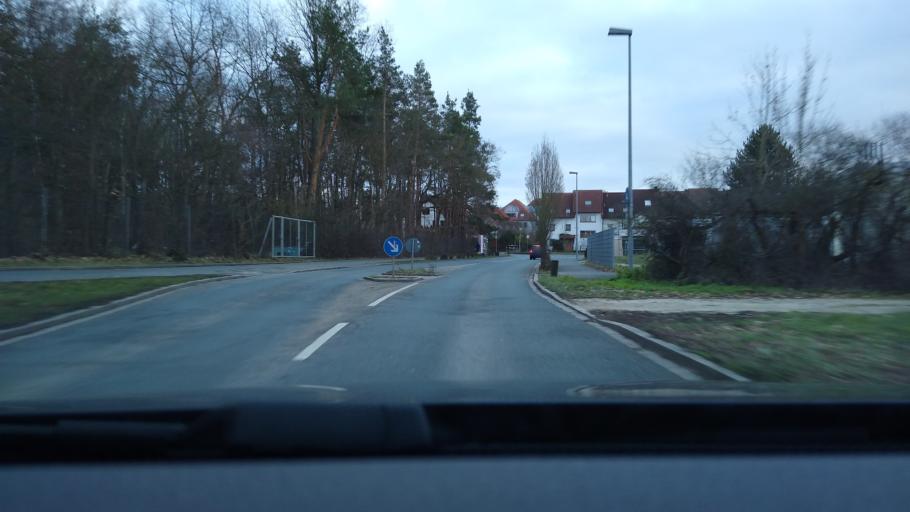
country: DE
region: Bavaria
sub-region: Regierungsbezirk Mittelfranken
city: Oberasbach
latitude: 49.4237
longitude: 10.9821
